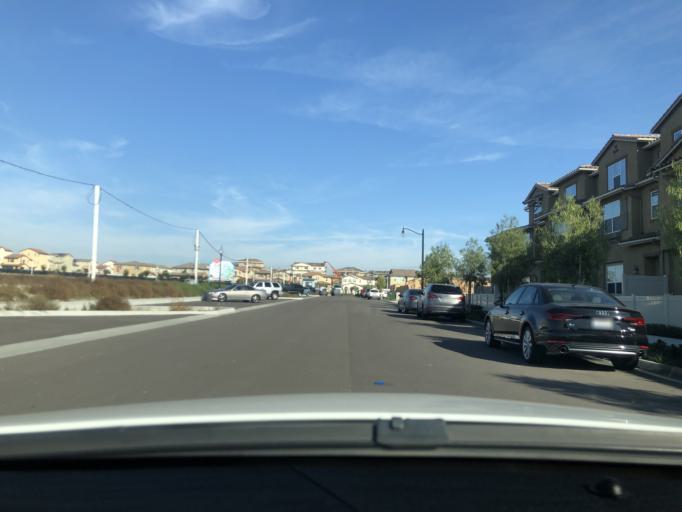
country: US
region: California
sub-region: San Diego County
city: Bonita
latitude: 32.6083
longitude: -116.9952
